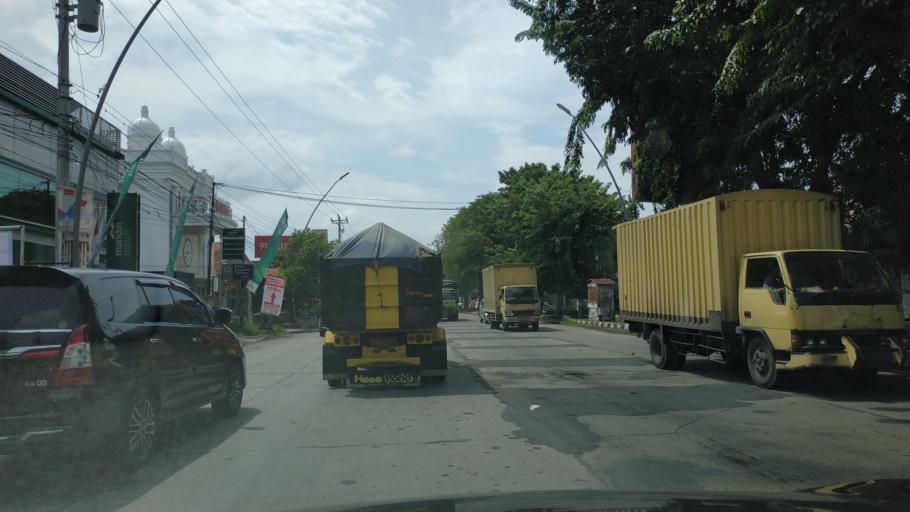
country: ID
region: Central Java
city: Tegal
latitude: -6.8662
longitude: 109.1336
